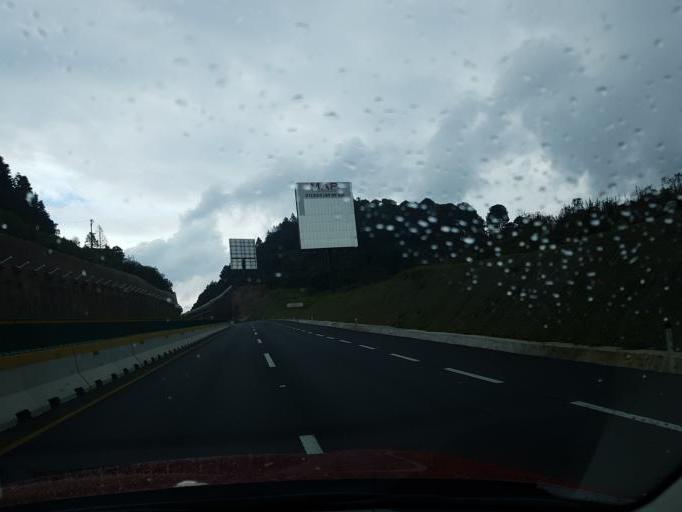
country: MX
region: Morelos
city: San Jeronimo Acazulco
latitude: 19.2986
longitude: -99.3977
